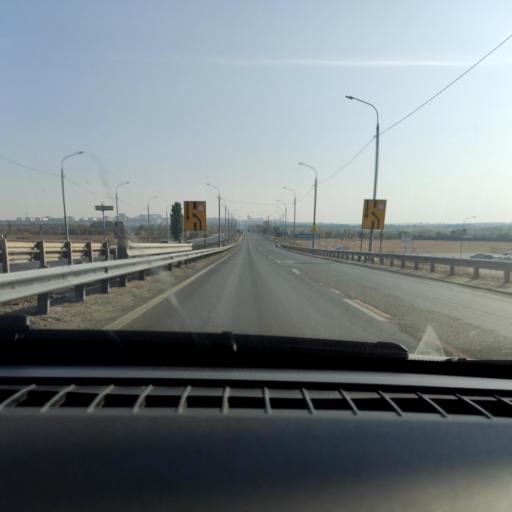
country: RU
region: Voronezj
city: Pridonskoy
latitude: 51.6517
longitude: 39.0578
